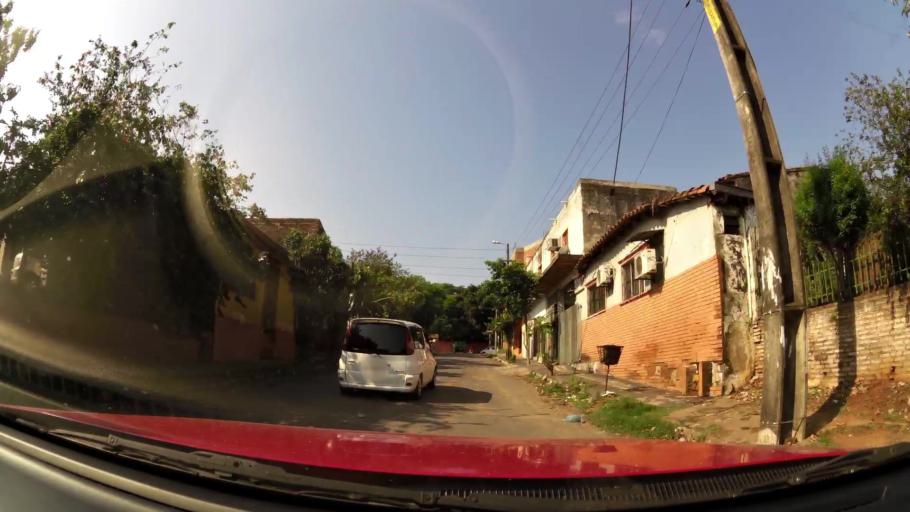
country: PY
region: Asuncion
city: Asuncion
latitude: -25.3125
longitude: -57.6362
